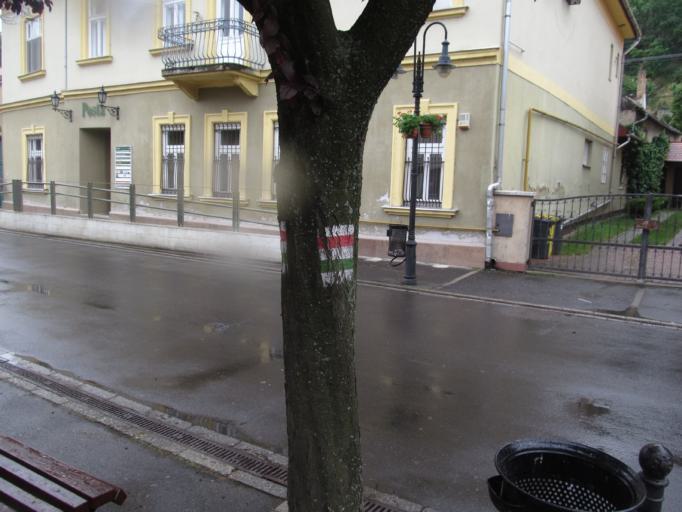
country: HU
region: Borsod-Abauj-Zemplen
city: Tokaj
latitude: 48.1234
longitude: 21.4111
